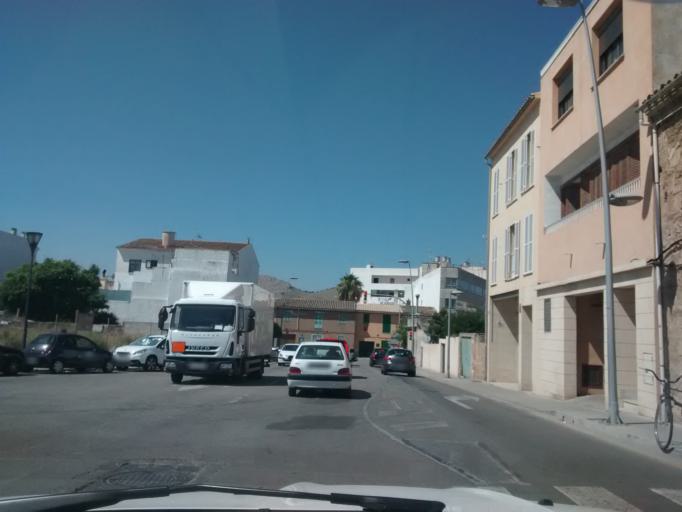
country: ES
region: Balearic Islands
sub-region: Illes Balears
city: Alcudia
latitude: 39.8523
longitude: 3.1260
